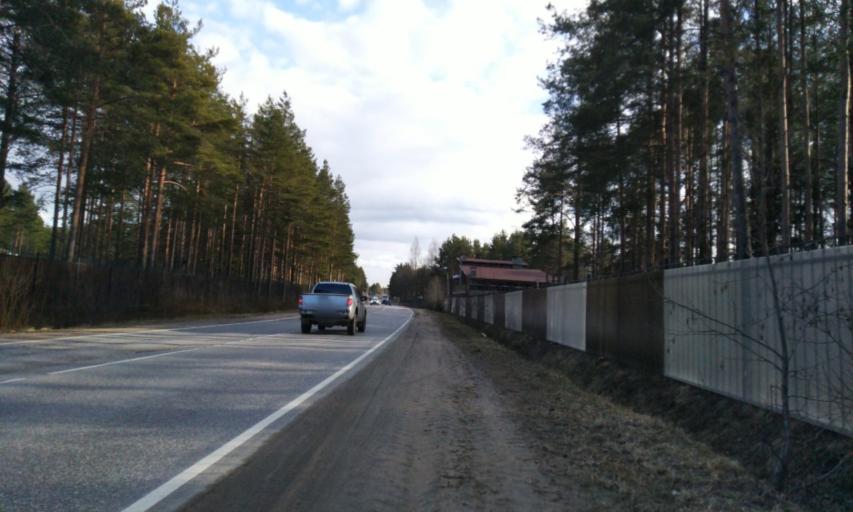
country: RU
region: Leningrad
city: Novoye Devyatkino
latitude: 60.1195
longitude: 30.4488
